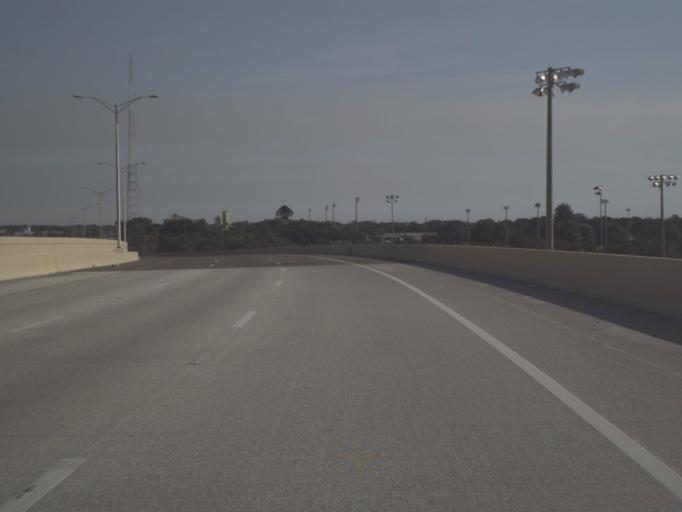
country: US
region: Florida
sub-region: Orange County
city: Fairview Shores
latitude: 28.5989
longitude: -81.4170
